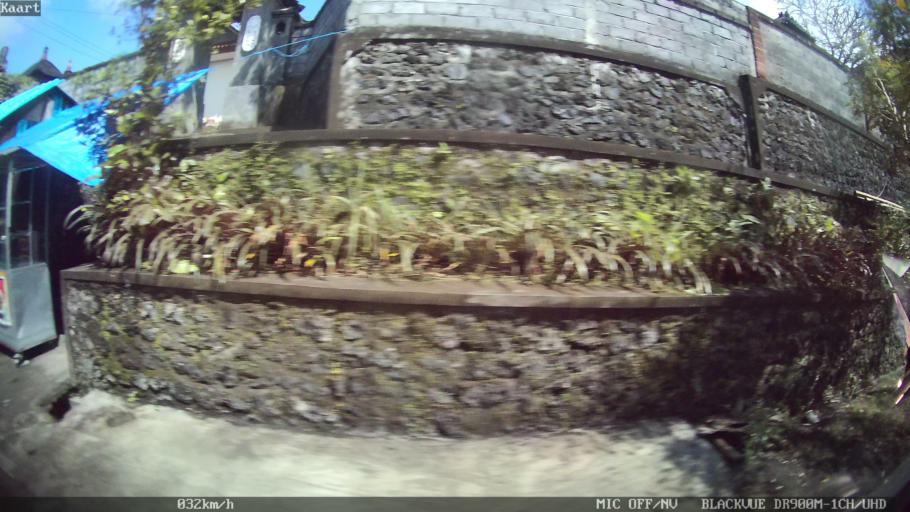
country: ID
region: Bali
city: Banjar Tebongkang
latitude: -8.5474
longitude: 115.2675
